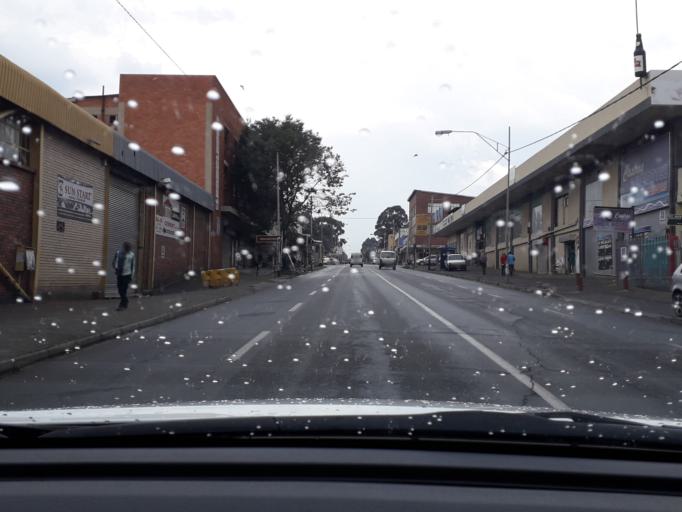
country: ZA
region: Gauteng
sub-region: City of Johannesburg Metropolitan Municipality
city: Johannesburg
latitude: -26.2386
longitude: 28.0305
